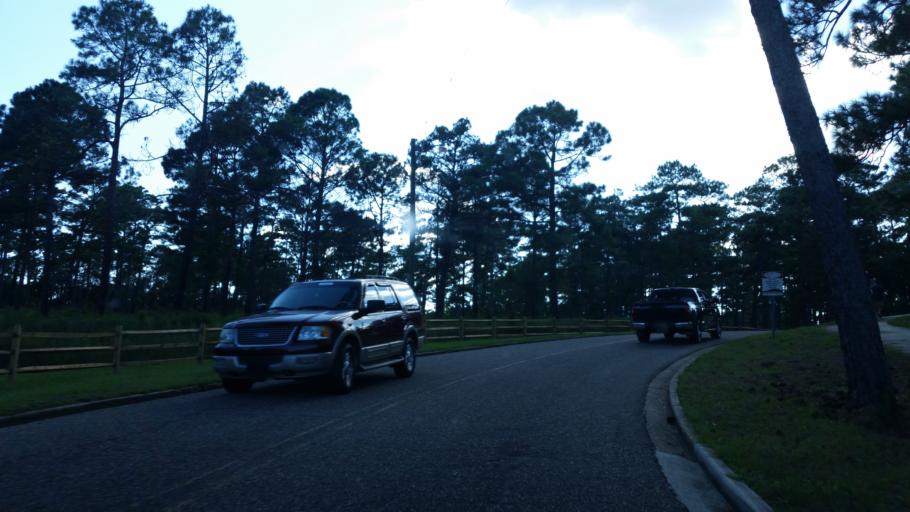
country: US
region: Alabama
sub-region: Mobile County
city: Prichard
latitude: 30.7033
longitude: -88.1562
